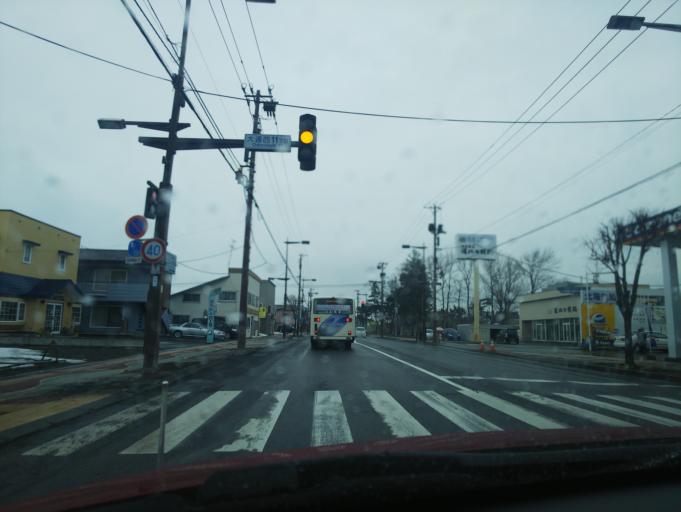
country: JP
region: Hokkaido
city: Nayoro
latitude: 44.1702
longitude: 142.3941
